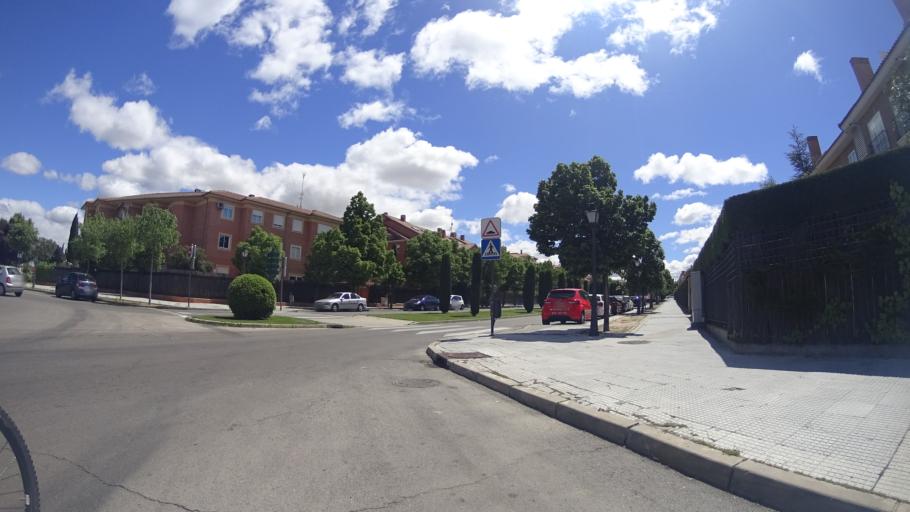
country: ES
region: Madrid
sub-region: Provincia de Madrid
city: Villaviciosa de Odon
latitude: 40.3631
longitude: -3.9139
